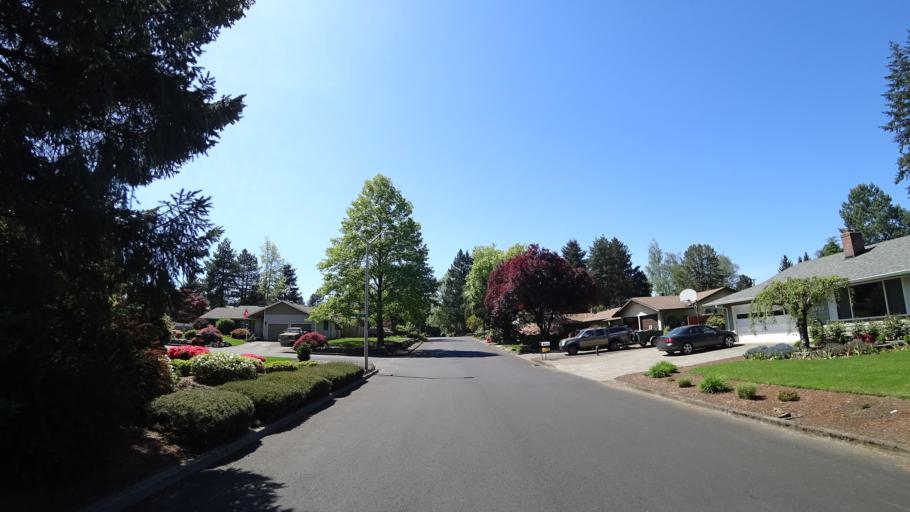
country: US
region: Oregon
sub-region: Washington County
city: Hillsboro
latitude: 45.5114
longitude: -122.9475
